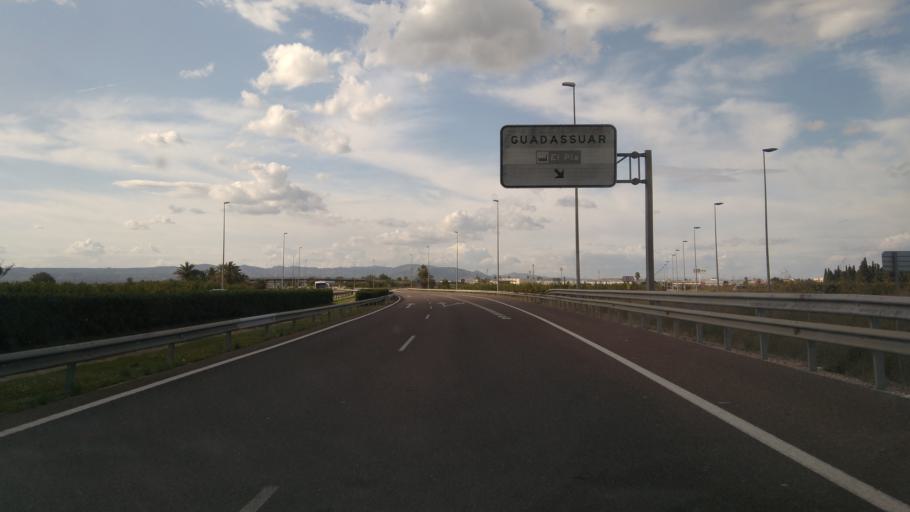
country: ES
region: Valencia
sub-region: Provincia de Valencia
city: Guadassuar
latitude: 39.1758
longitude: -0.4703
